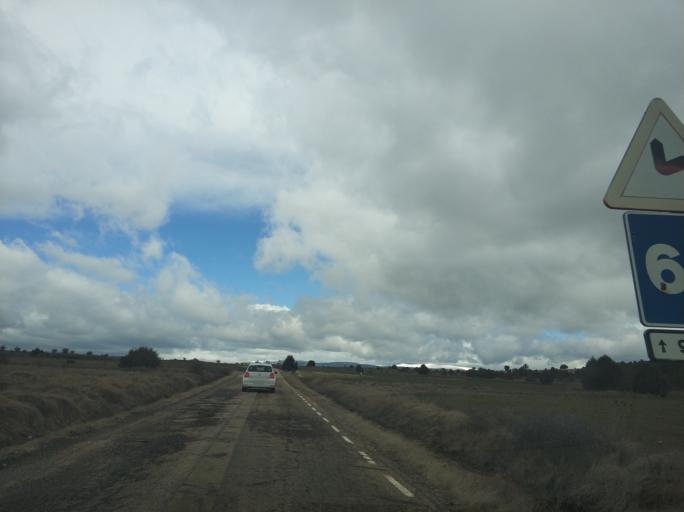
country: ES
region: Castille and Leon
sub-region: Provincia de Soria
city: Abejar
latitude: 41.7951
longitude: -2.7684
